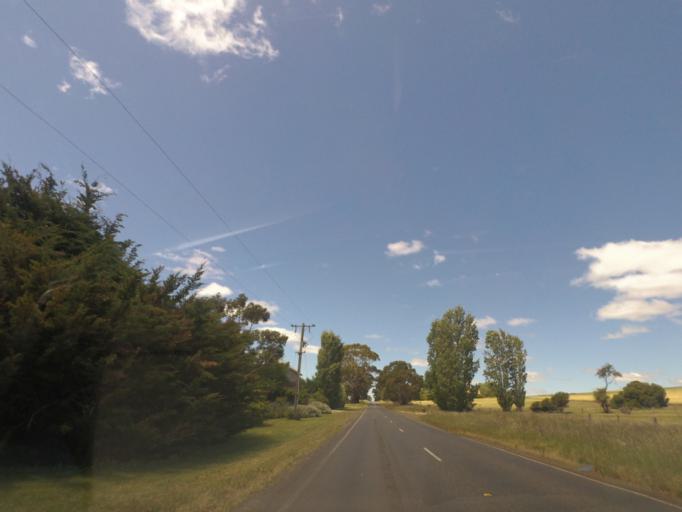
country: AU
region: Victoria
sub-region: Mount Alexander
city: Castlemaine
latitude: -37.3227
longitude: 144.1972
